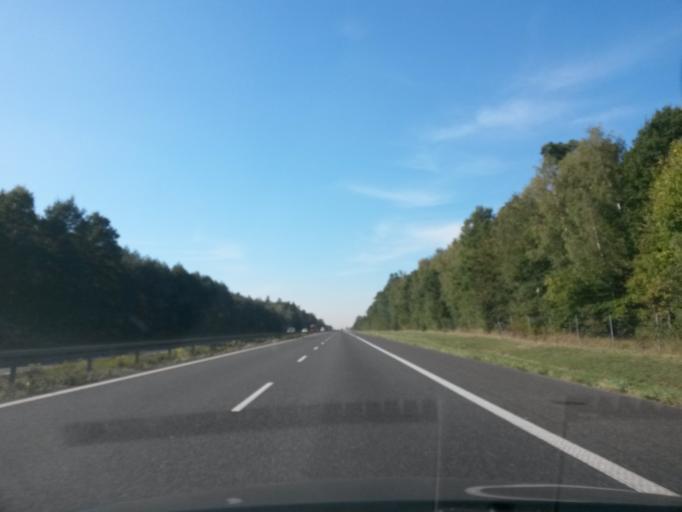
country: PL
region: Silesian Voivodeship
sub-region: Powiat gliwicki
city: Toszek
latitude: 50.3674
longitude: 18.5015
